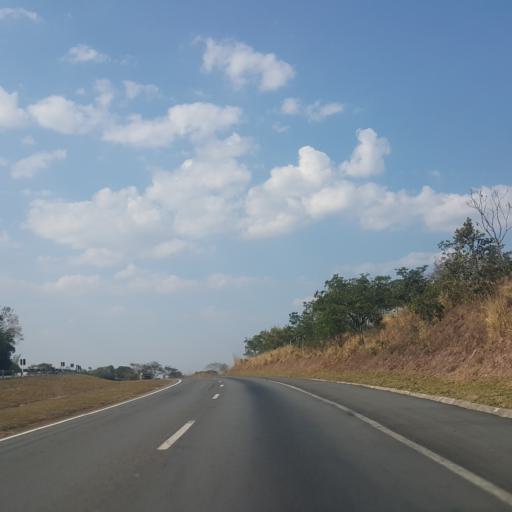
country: BR
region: Goias
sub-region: Abadiania
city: Abadiania
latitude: -16.1668
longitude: -48.6350
